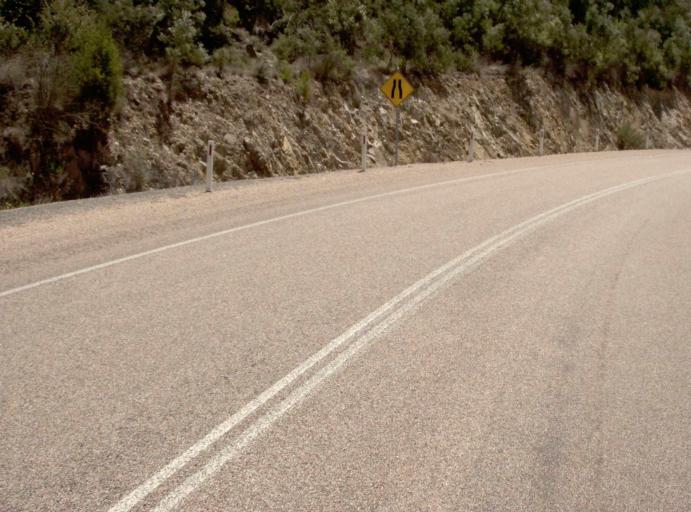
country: AU
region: Victoria
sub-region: East Gippsland
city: Lakes Entrance
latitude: -37.5642
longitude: 147.8876
